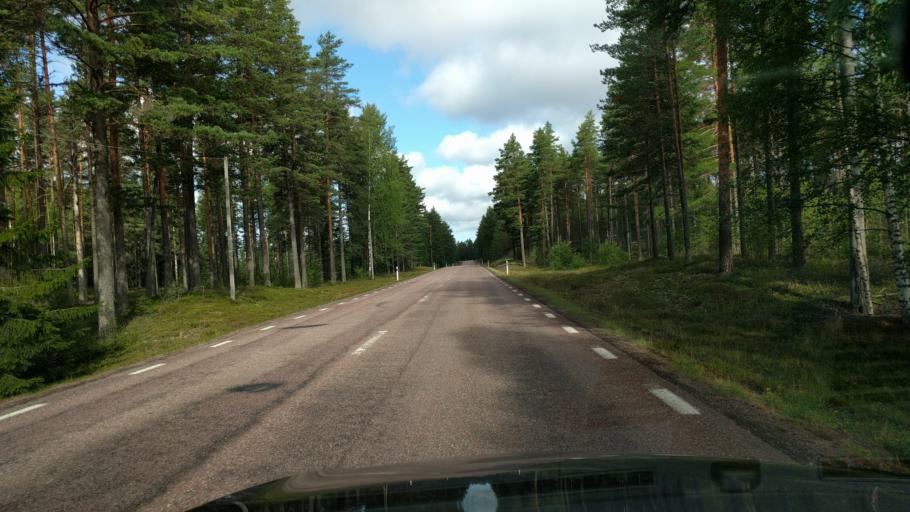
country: SE
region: Dalarna
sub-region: Mora Kommun
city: Mora
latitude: 61.0665
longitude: 14.3893
